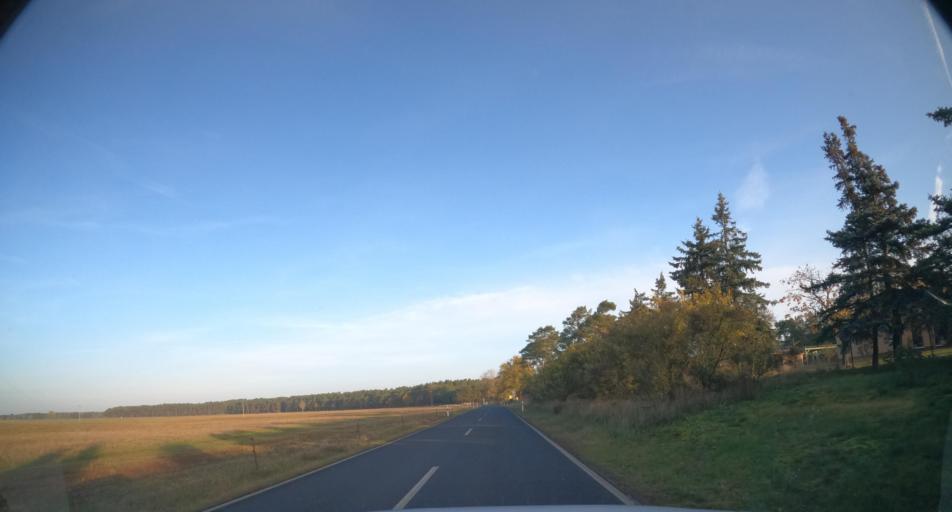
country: DE
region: Mecklenburg-Vorpommern
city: Ahlbeck
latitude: 53.6735
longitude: 14.1904
